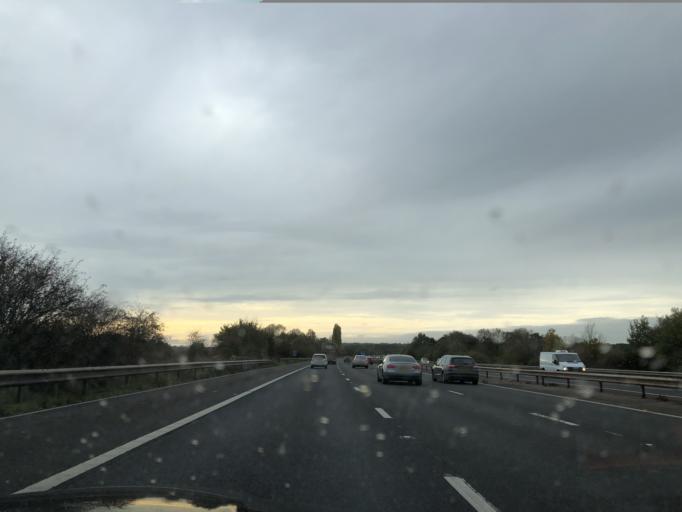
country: GB
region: England
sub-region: Hampshire
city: Odiham
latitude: 51.2777
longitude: -0.9307
